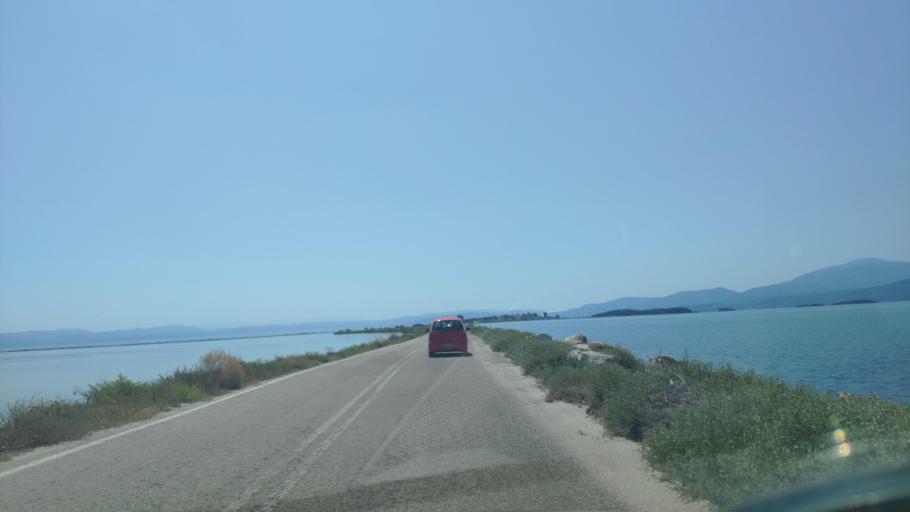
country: GR
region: Epirus
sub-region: Nomos Artas
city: Aneza
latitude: 39.0313
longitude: 20.8973
